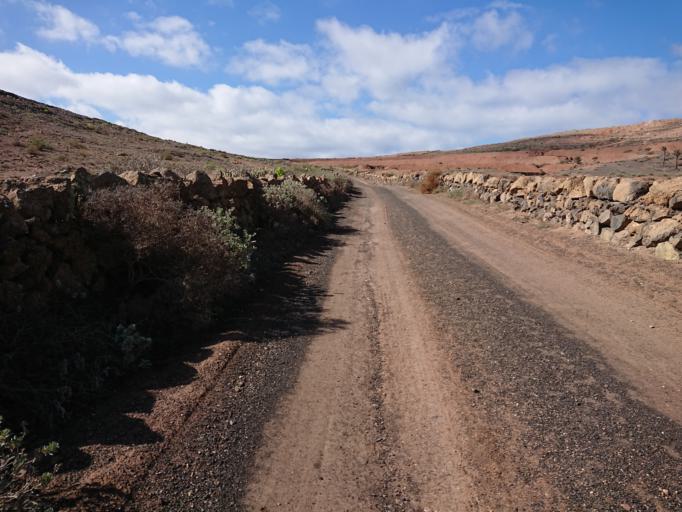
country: ES
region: Canary Islands
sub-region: Provincia de Las Palmas
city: Haria
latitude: 29.1456
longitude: -13.5155
